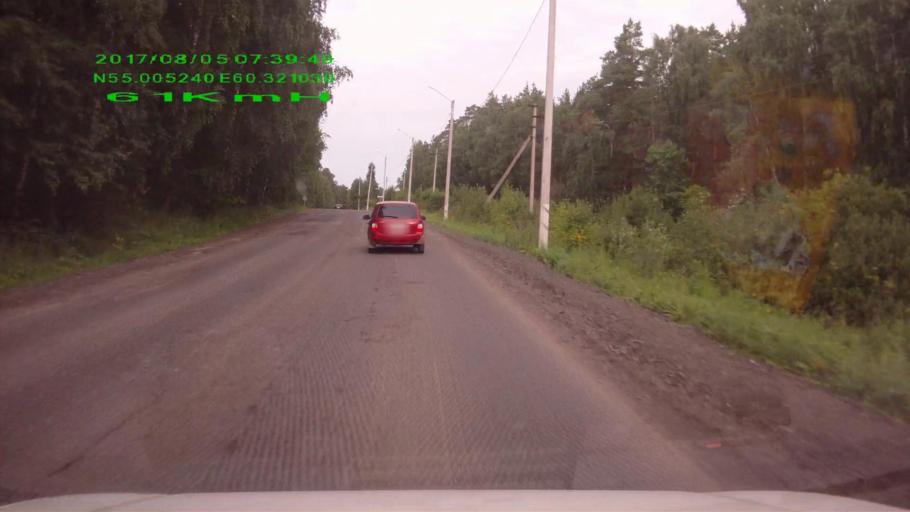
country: RU
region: Chelyabinsk
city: Chebarkul'
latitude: 55.0053
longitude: 60.3207
